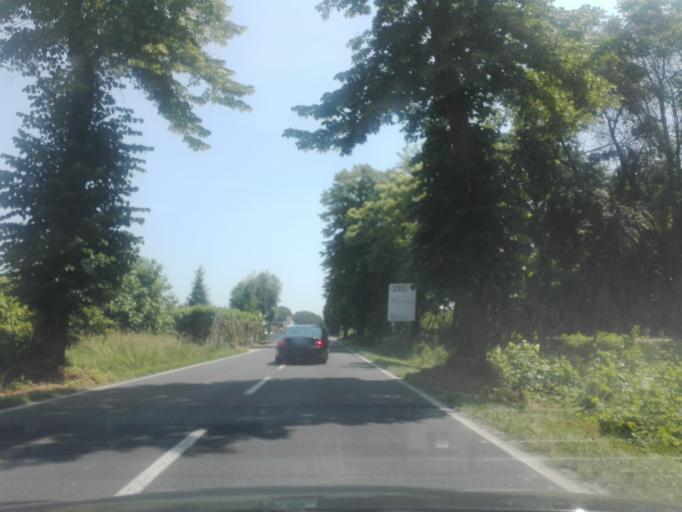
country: IT
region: Veneto
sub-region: Provincia di Rovigo
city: Adria
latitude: 45.0613
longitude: 12.0269
